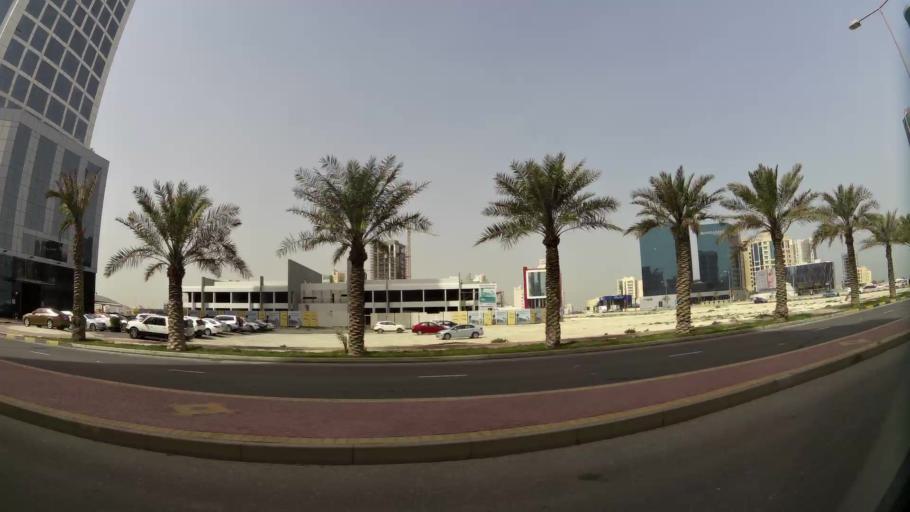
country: BH
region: Manama
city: Jidd Hafs
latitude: 26.2370
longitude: 50.5372
